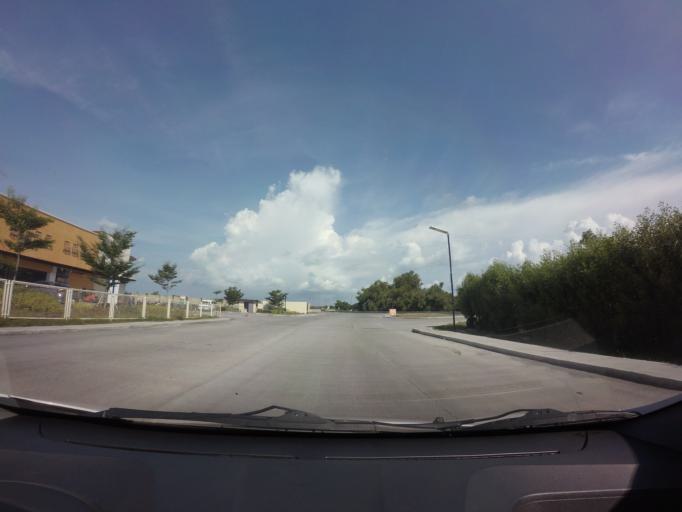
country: PH
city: Sambayanihan People's Village
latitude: 14.4760
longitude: 120.9842
